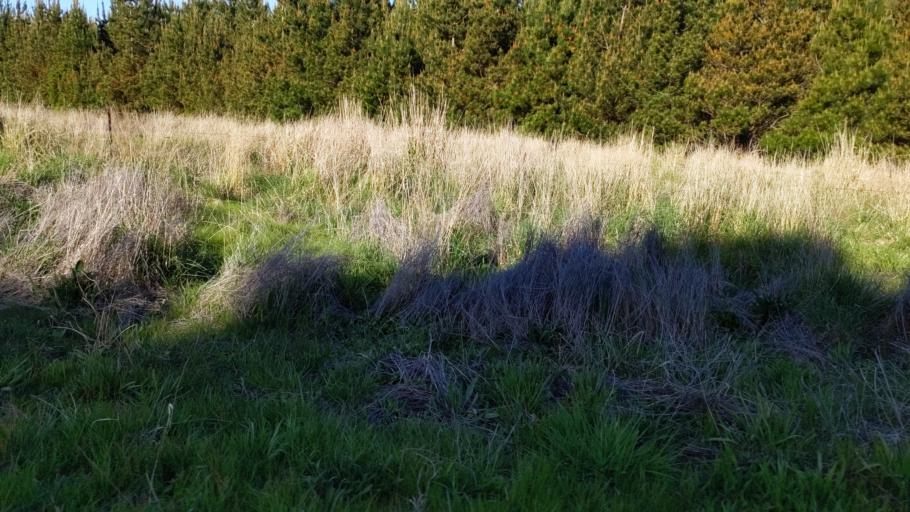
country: AU
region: New South Wales
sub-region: Blayney
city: Millthorpe
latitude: -33.4151
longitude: 149.3019
